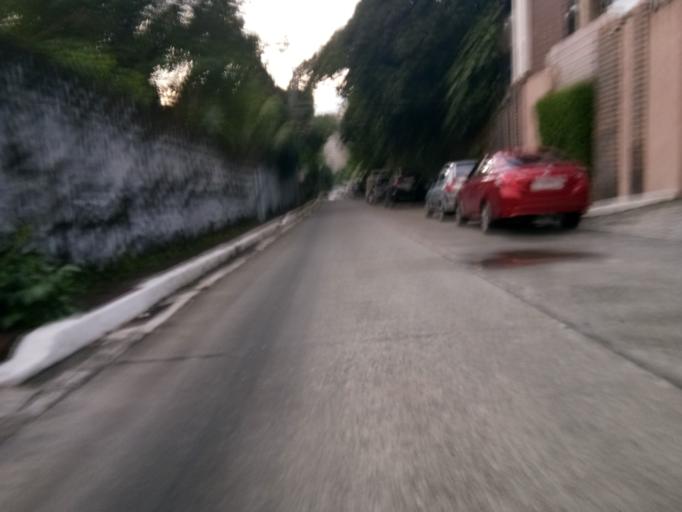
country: PH
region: Metro Manila
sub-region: San Juan
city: San Juan
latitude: 14.6104
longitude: 121.0411
